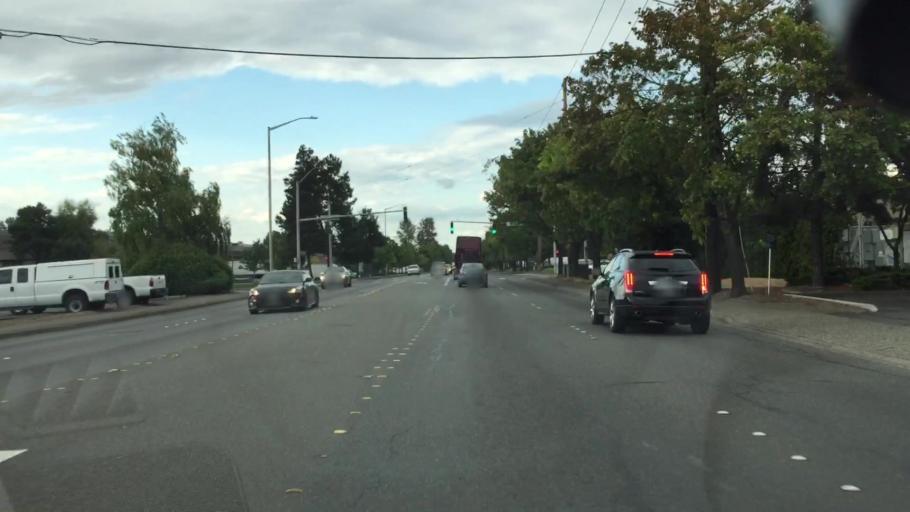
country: US
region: Washington
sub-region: King County
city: Kent
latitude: 47.4148
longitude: -122.2279
